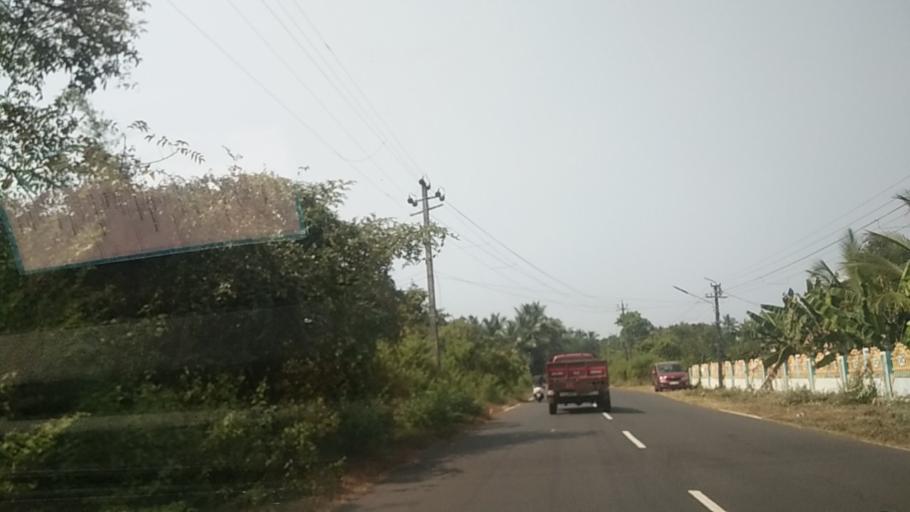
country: IN
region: Goa
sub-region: North Goa
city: Morjim
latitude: 15.6567
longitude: 73.7484
